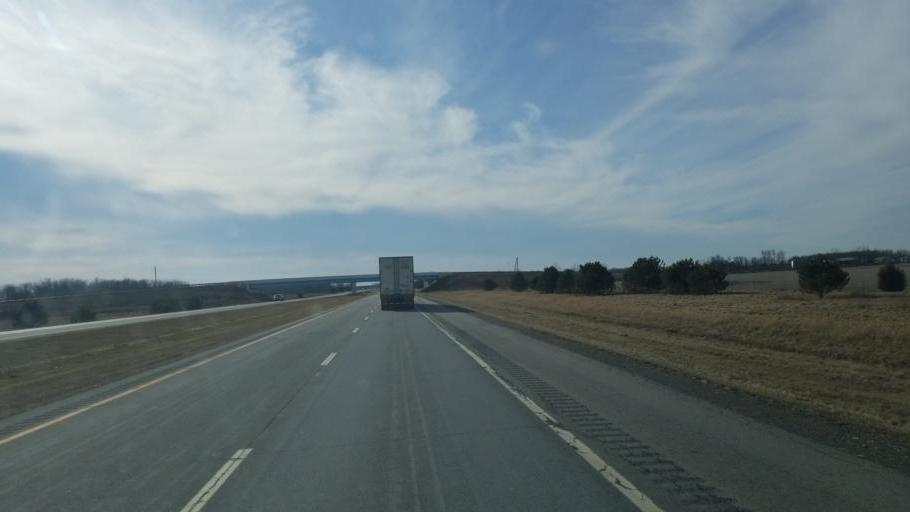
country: US
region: Ohio
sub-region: Allen County
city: Delphos
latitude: 40.8735
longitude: -84.3628
